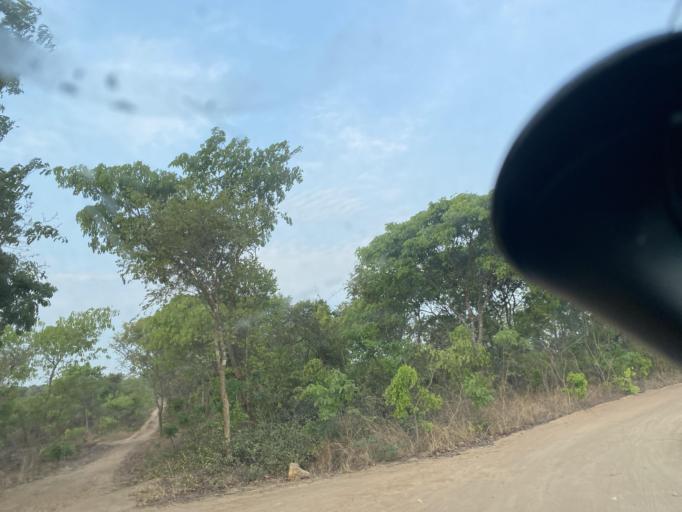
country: ZM
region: Lusaka
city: Chongwe
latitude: -15.2044
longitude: 28.5107
